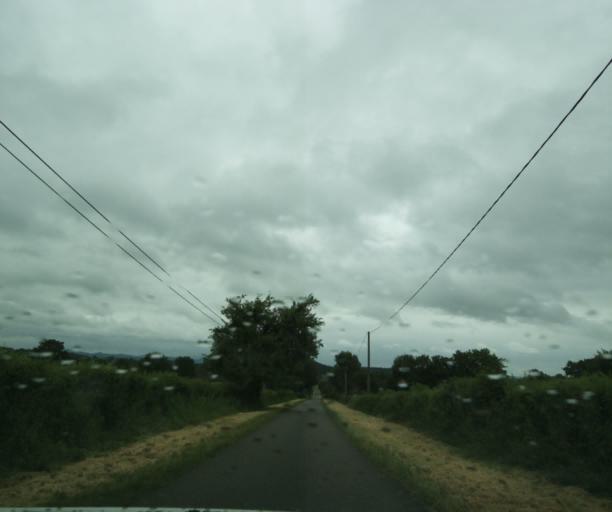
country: FR
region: Bourgogne
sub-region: Departement de Saone-et-Loire
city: Charolles
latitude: 46.4860
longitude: 4.2713
